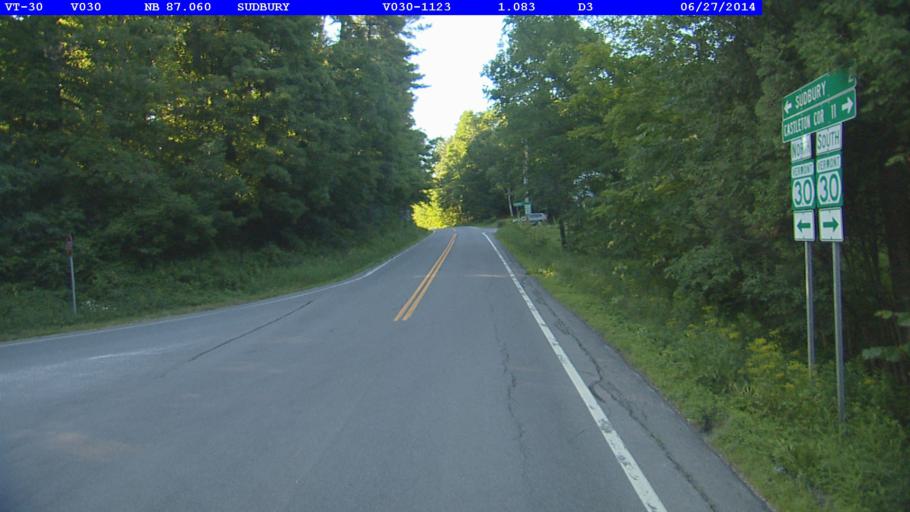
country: US
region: Vermont
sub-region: Rutland County
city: Brandon
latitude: 43.7648
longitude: -73.1967
